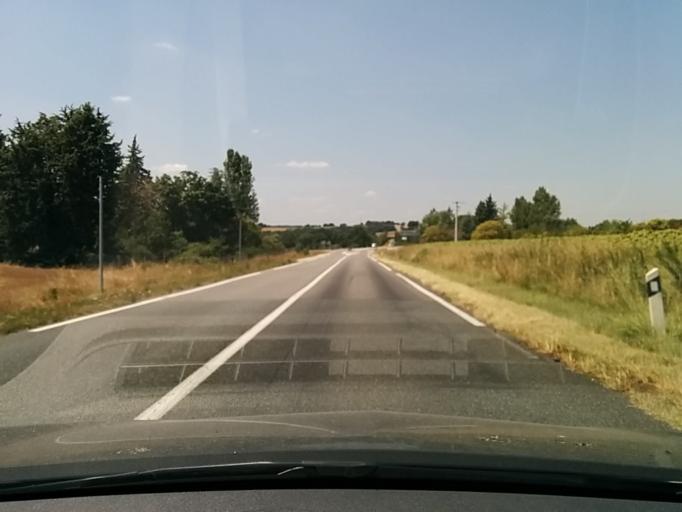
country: FR
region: Midi-Pyrenees
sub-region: Departement du Gers
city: Gimont
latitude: 43.6073
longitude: 0.9798
